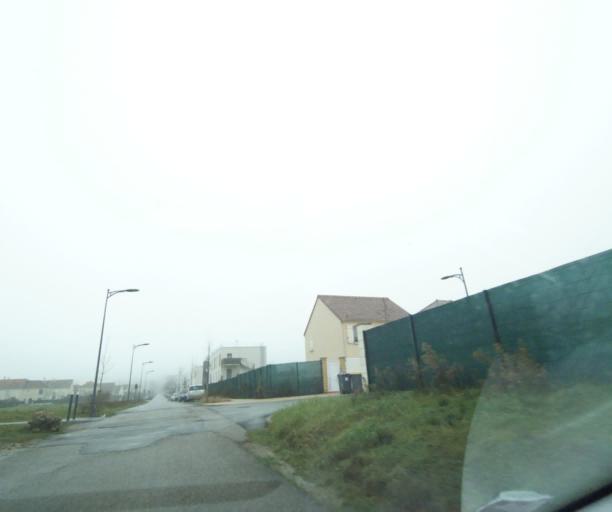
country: FR
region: Ile-de-France
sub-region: Departement de Seine-et-Marne
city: Othis
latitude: 49.0652
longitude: 2.6766
